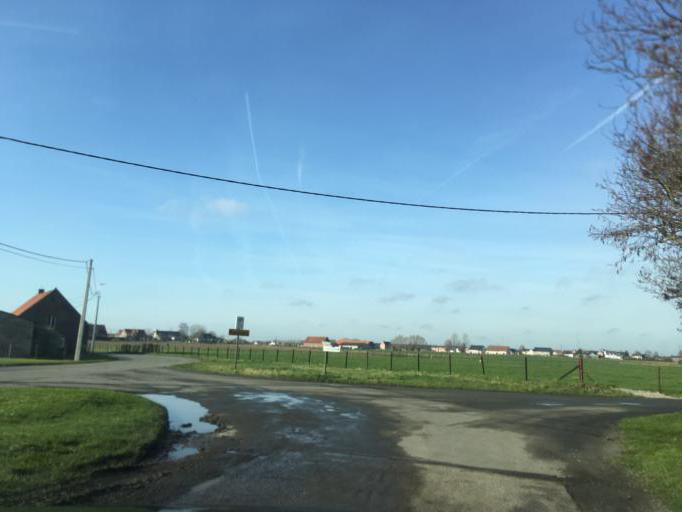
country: BE
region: Flanders
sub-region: Provincie West-Vlaanderen
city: Ardooie
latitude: 50.9525
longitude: 3.1718
